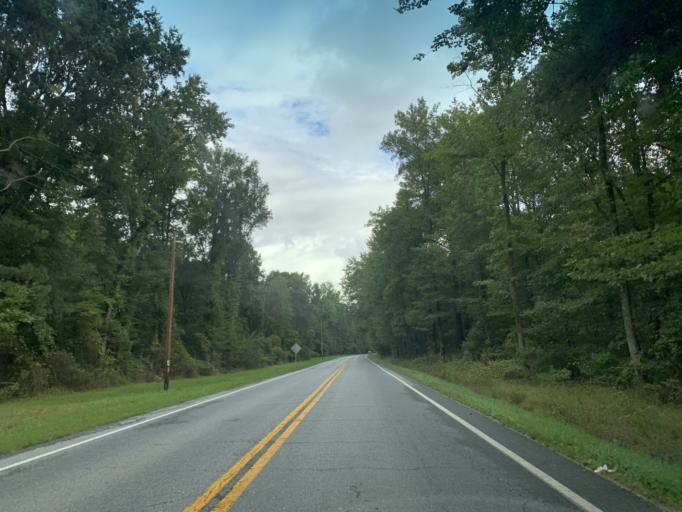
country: US
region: Maryland
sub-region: Caroline County
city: Greensboro
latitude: 39.0454
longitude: -75.8646
